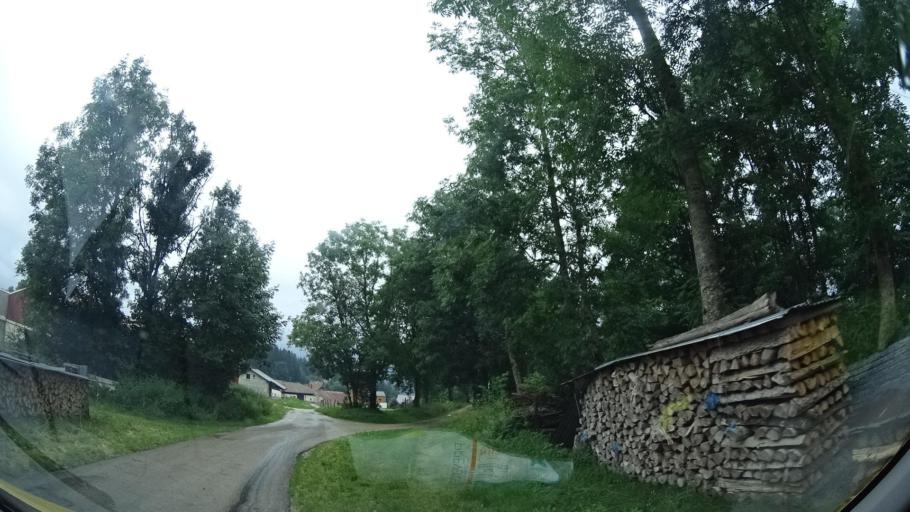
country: FR
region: Franche-Comte
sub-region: Departement du Doubs
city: Les Fourgs
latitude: 46.8259
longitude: 6.3461
